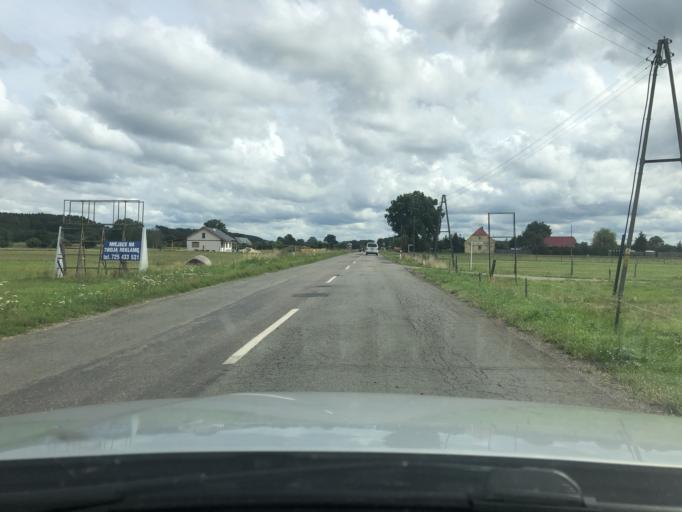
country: PL
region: Lubusz
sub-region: Powiat strzelecko-drezdenecki
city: Drezdenko
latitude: 52.8428
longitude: 15.8842
